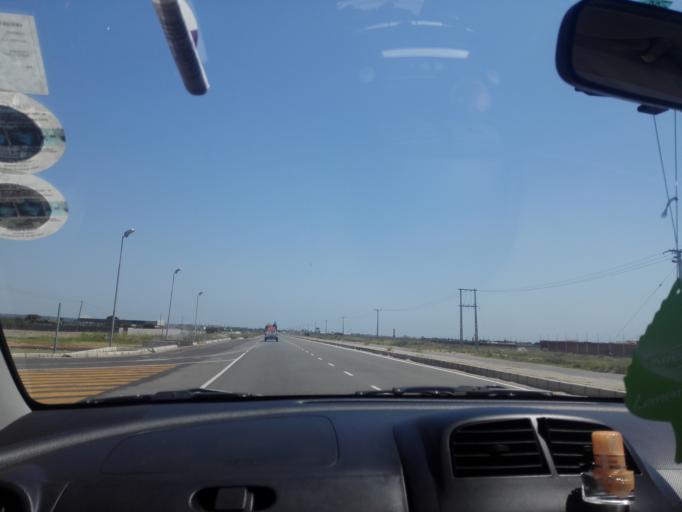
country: MZ
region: Maputo City
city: Maputo
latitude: -25.8425
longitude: 32.6714
